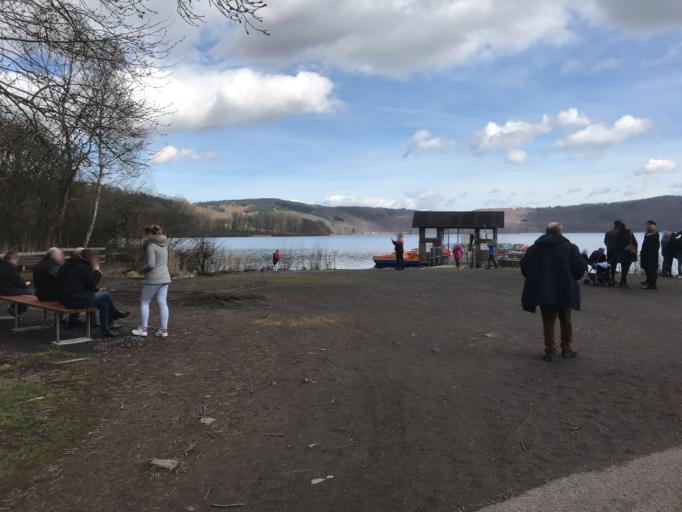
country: DE
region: Rheinland-Pfalz
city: Glees
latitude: 50.4063
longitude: 7.2564
